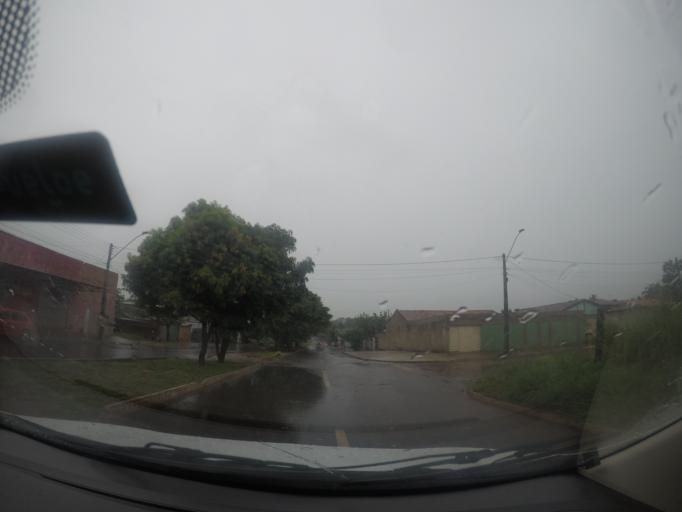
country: BR
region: Goias
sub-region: Goiania
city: Goiania
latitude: -16.5958
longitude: -49.3253
